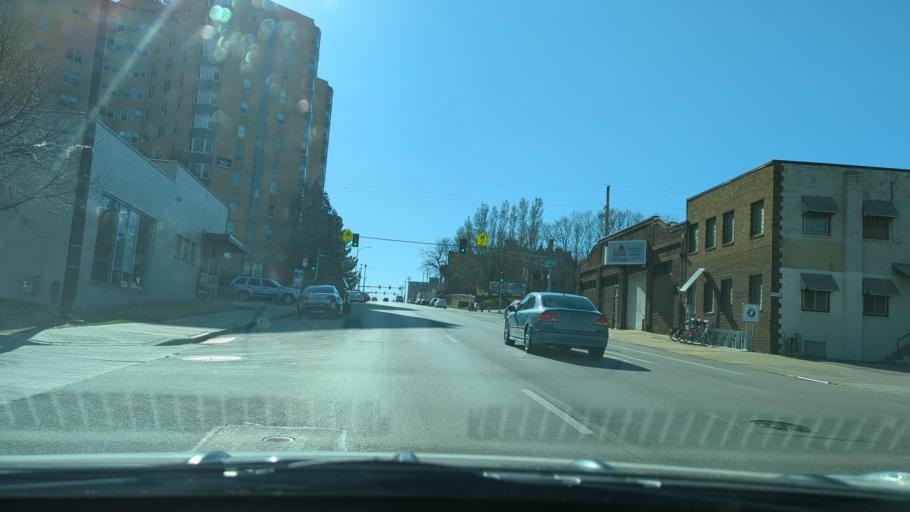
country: US
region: Nebraska
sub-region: Douglas County
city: Omaha
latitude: 41.2542
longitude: -95.9439
